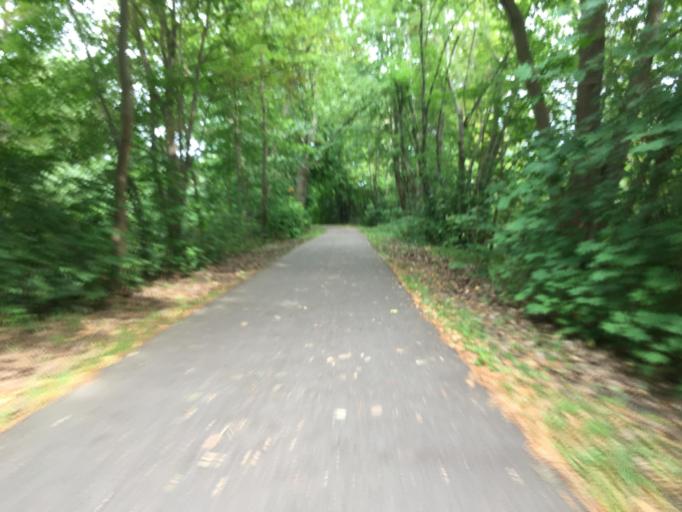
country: DE
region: Brandenburg
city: Prenzlau
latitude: 53.3020
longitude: 13.8455
